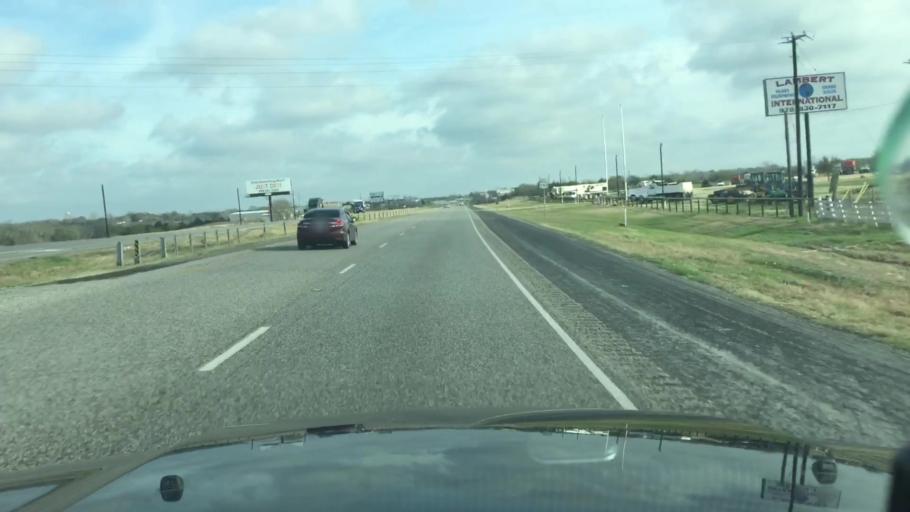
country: US
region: Texas
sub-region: Washington County
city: Brenham
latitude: 30.1409
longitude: -96.2819
